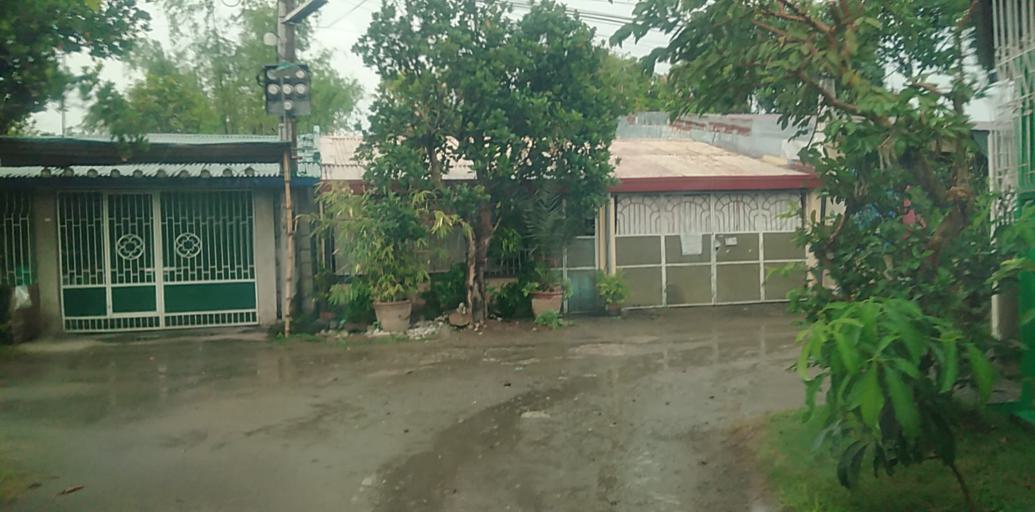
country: PH
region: Central Luzon
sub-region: Province of Pampanga
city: Arenas
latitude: 15.1727
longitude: 120.6828
